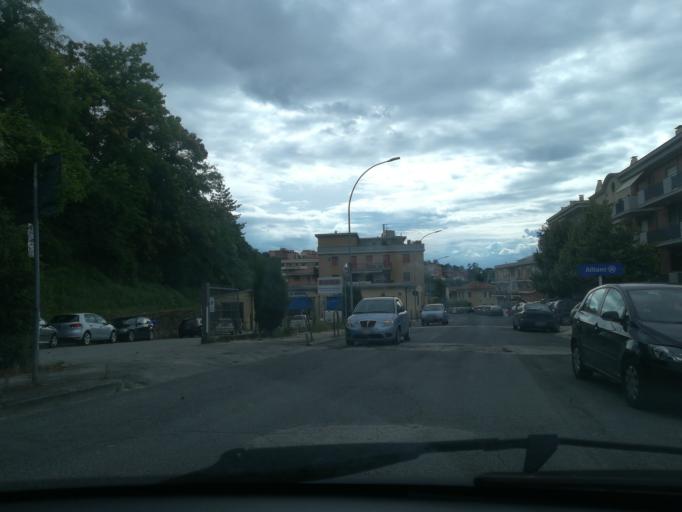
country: IT
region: The Marches
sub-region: Provincia di Macerata
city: Macerata
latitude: 43.3017
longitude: 13.4358
